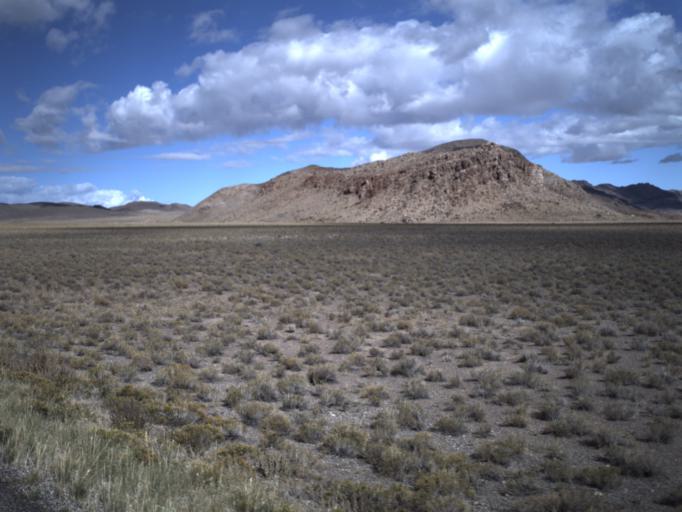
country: US
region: Utah
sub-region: Beaver County
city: Milford
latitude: 38.5753
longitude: -113.7983
